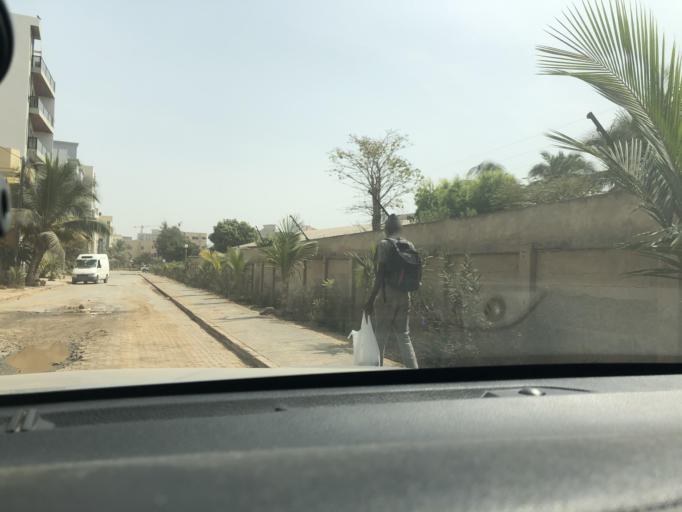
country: SN
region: Dakar
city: Mermoz Boabab
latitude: 14.7454
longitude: -17.5173
